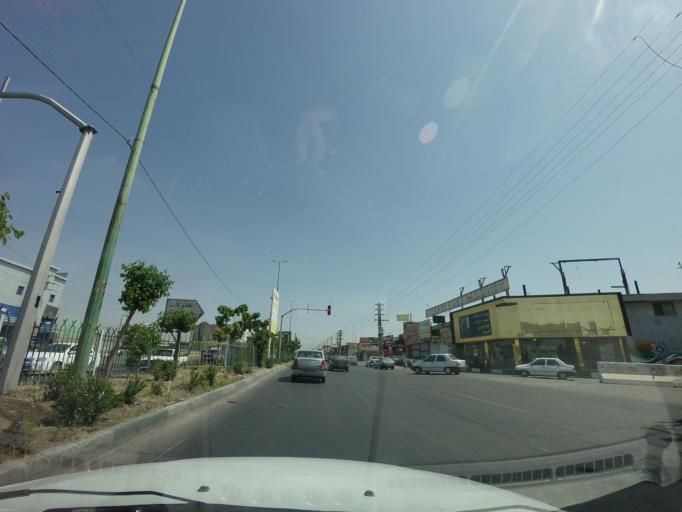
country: IR
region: Tehran
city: Eslamshahr
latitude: 35.6005
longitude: 51.3000
